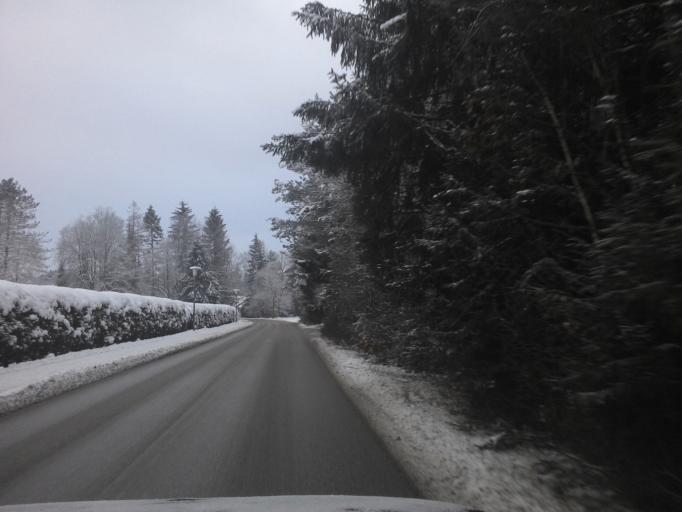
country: DE
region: Bavaria
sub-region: Upper Bavaria
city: Seeshaupt
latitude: 47.8196
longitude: 11.2902
